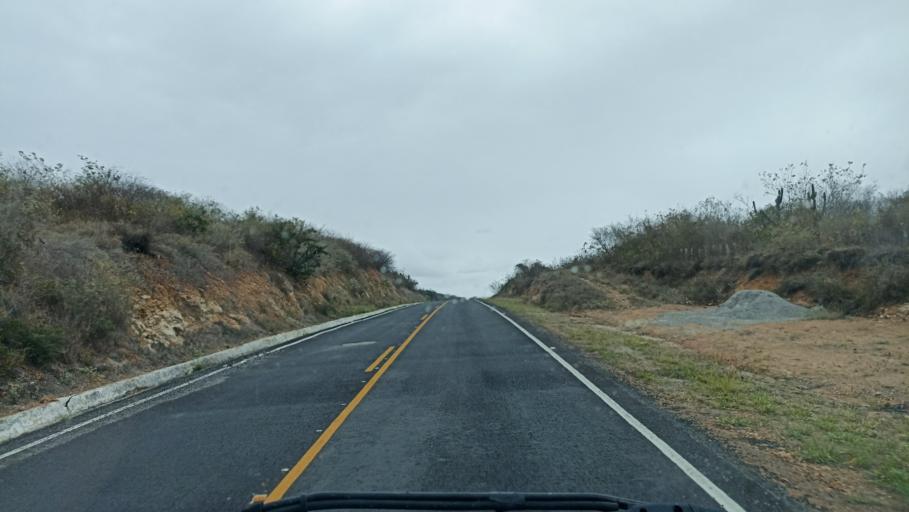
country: BR
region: Bahia
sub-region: Andarai
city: Vera Cruz
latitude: -13.0464
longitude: -40.7669
